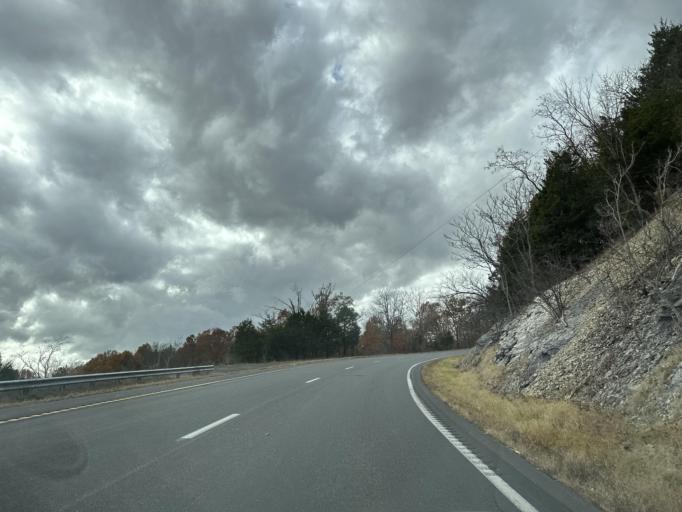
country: US
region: Virginia
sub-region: Shenandoah County
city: Strasburg
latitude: 38.9762
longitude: -78.3925
